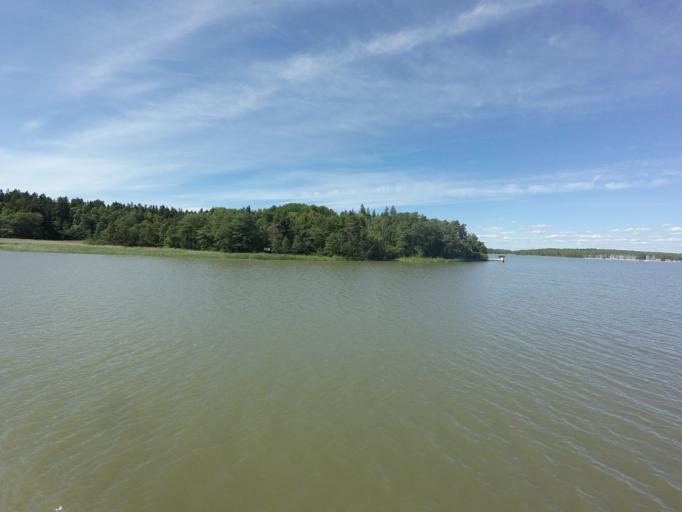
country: FI
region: Varsinais-Suomi
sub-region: Turku
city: Raisio
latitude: 60.4147
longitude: 22.1544
